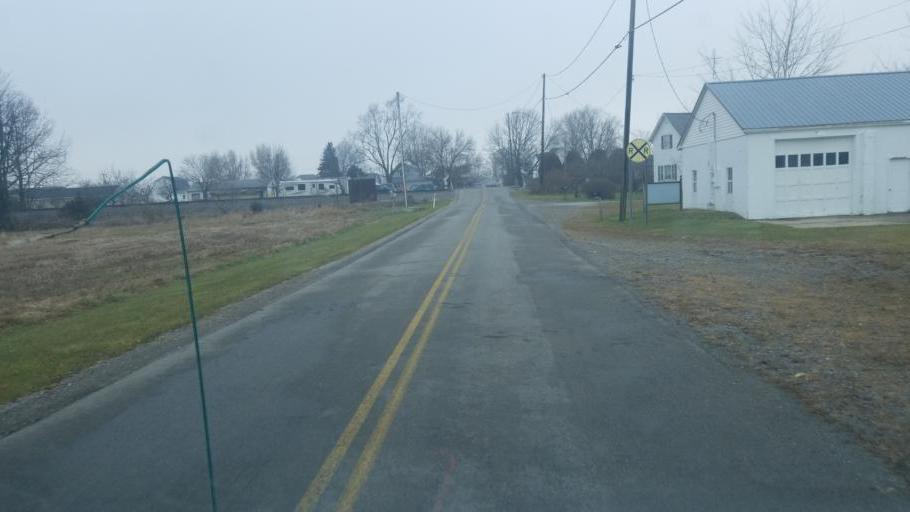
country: US
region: Ohio
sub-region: Hardin County
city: Kenton
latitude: 40.5311
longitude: -83.5250
